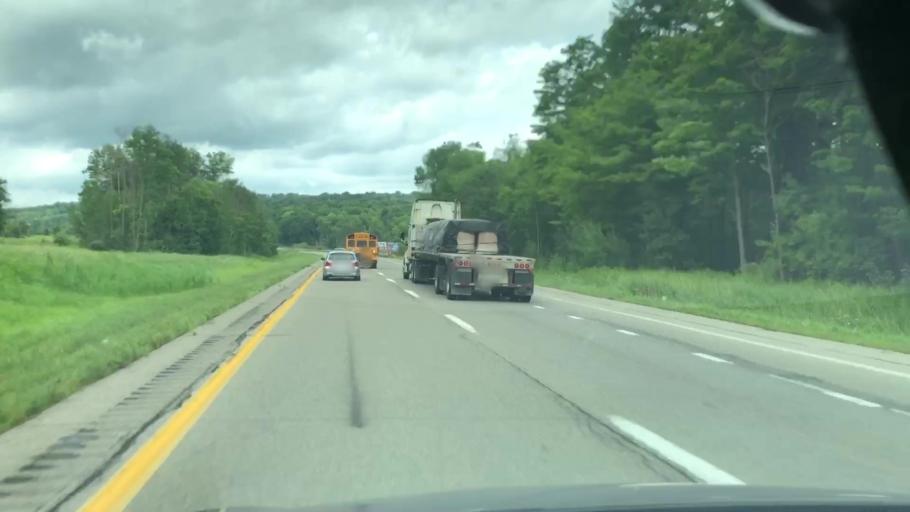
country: US
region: Pennsylvania
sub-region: Erie County
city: Edinboro
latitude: 41.8471
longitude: -80.1753
